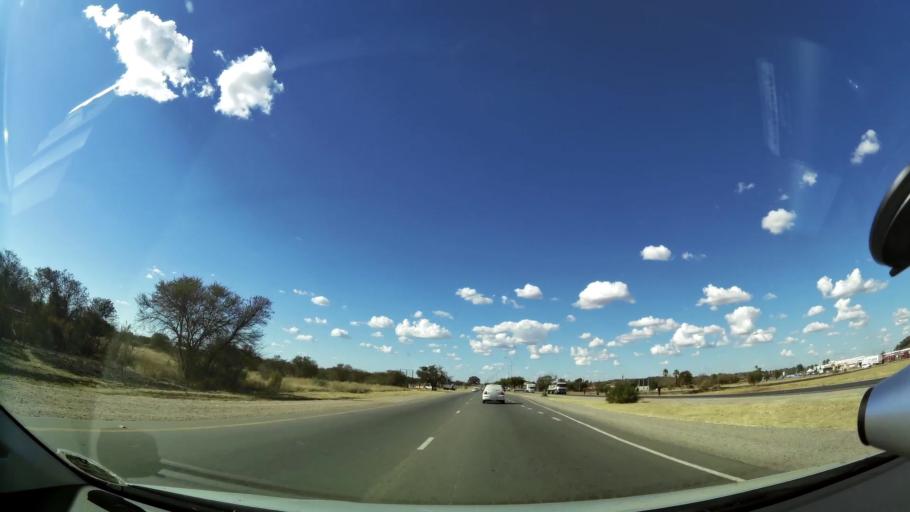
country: ZA
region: North-West
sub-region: Dr Kenneth Kaunda District Municipality
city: Klerksdorp
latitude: -26.8690
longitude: 26.6242
